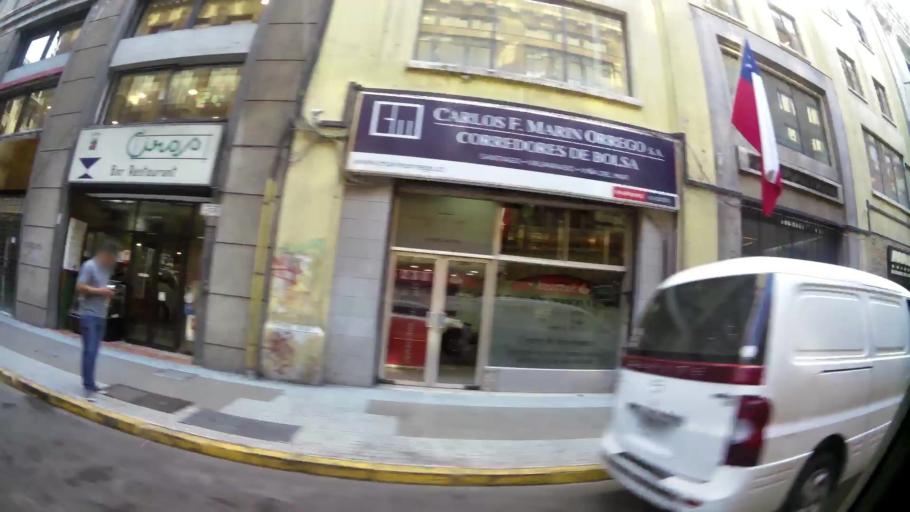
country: CL
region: Santiago Metropolitan
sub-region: Provincia de Santiago
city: Santiago
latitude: -33.4405
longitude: -70.6523
